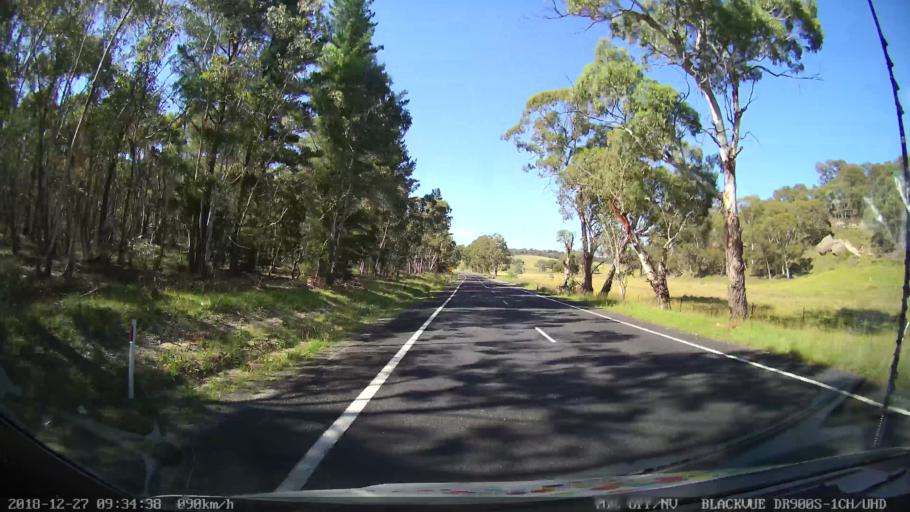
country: AU
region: New South Wales
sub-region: Lithgow
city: Portland
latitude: -33.2287
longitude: 150.0271
